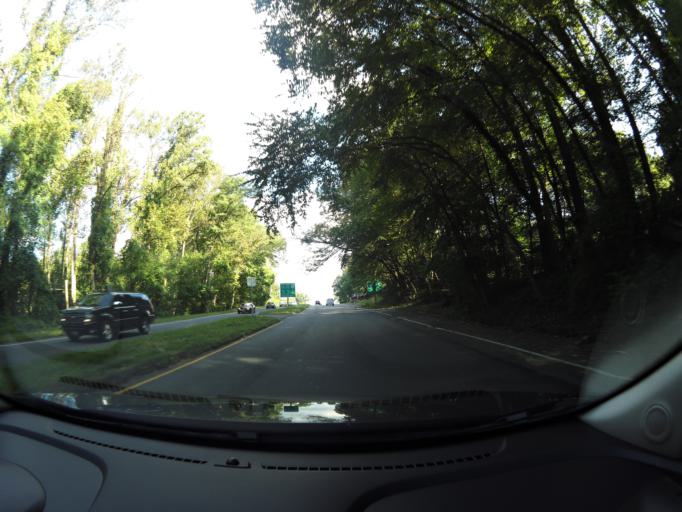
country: US
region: Virginia
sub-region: Fairfax County
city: McLean
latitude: 38.9558
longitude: -77.1976
